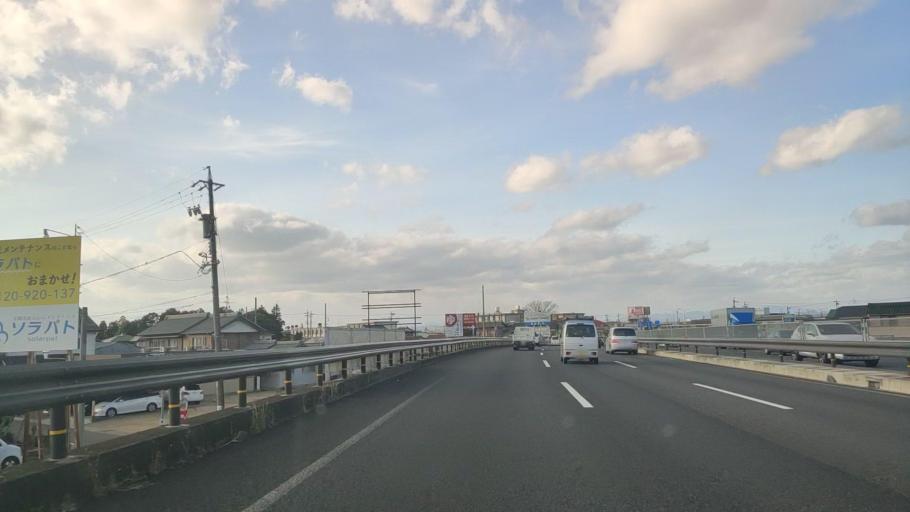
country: JP
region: Aichi
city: Kuroda
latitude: 35.3588
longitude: 136.7841
